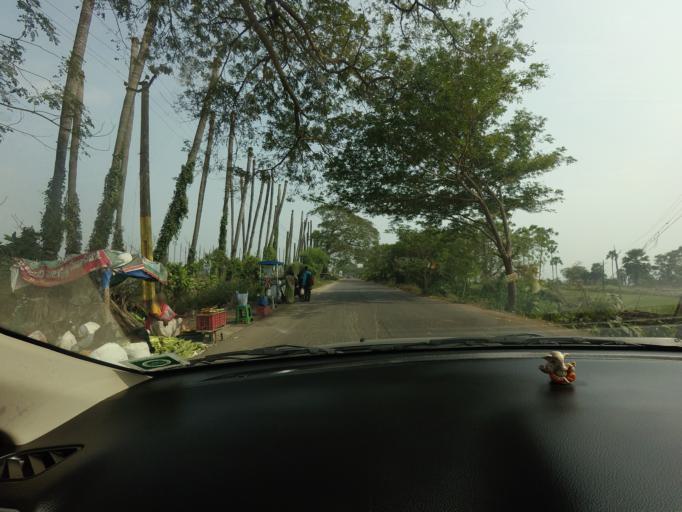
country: IN
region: Andhra Pradesh
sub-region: Krishna
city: Kankipadu
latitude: 16.4546
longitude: 80.7797
